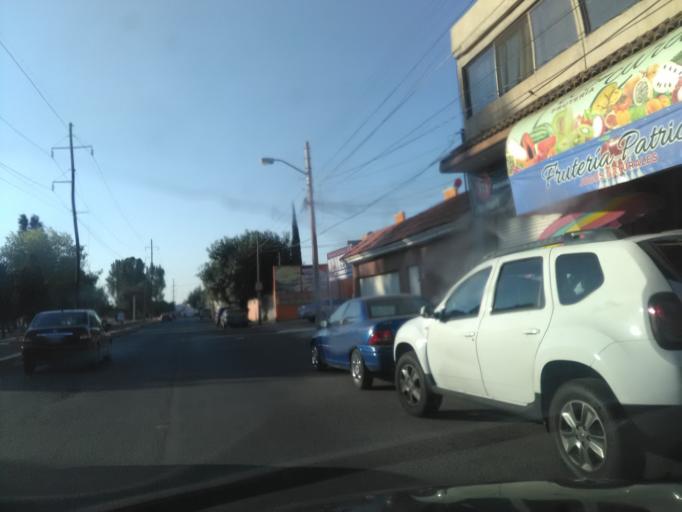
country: MX
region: Durango
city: Victoria de Durango
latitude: 24.0433
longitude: -104.6348
